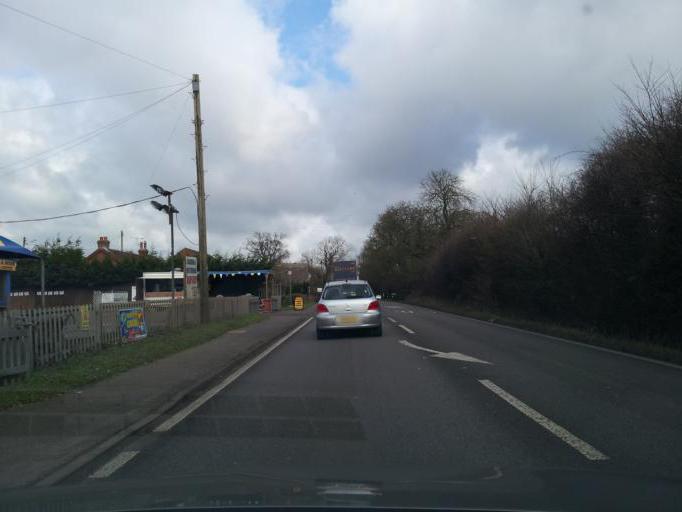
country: GB
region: England
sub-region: Suffolk
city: Needham Market
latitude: 52.1980
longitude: 1.0990
